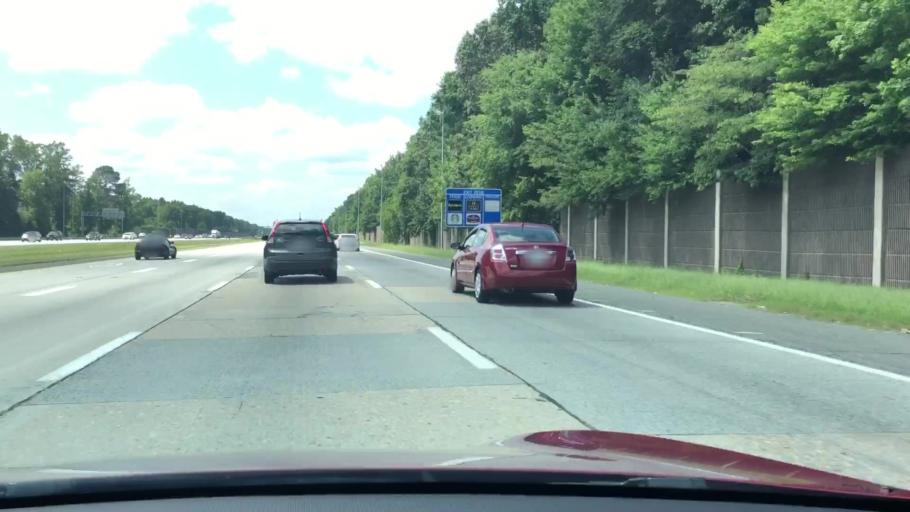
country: US
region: Virginia
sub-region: City of Chesapeake
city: Chesapeake
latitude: 36.7936
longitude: -76.2169
